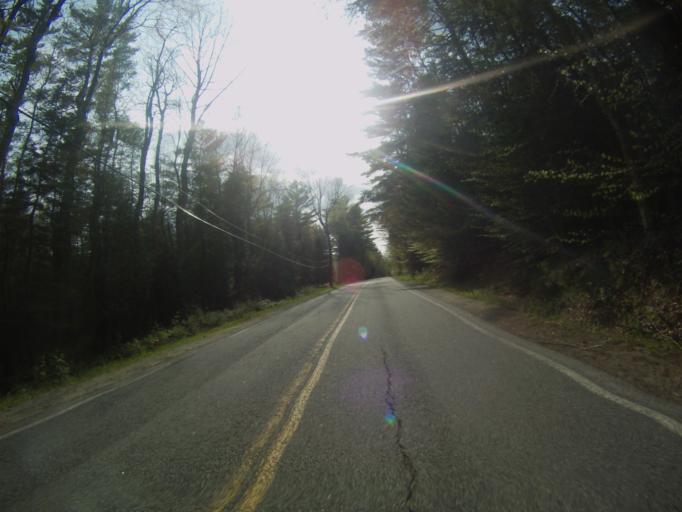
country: US
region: New York
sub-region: Warren County
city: Warrensburg
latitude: 43.8453
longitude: -73.8058
